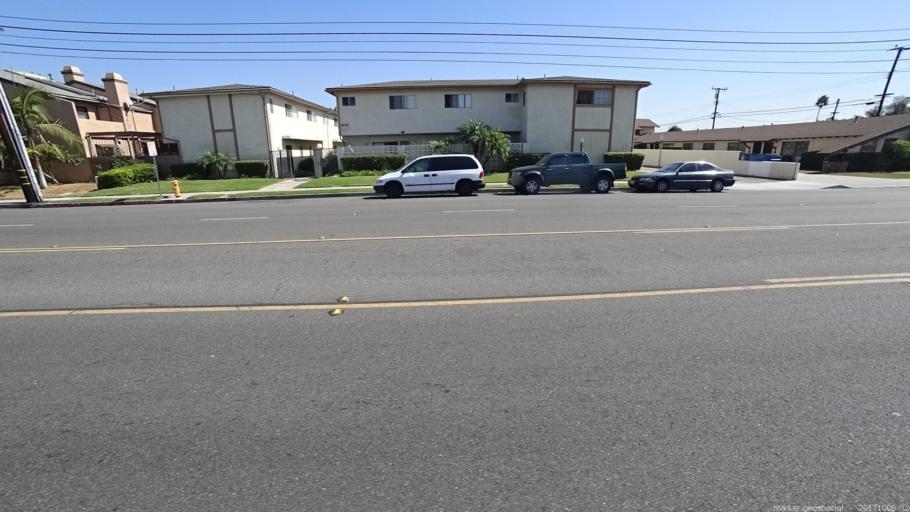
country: US
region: California
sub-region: Orange County
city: Stanton
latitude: 33.7980
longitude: -117.9845
